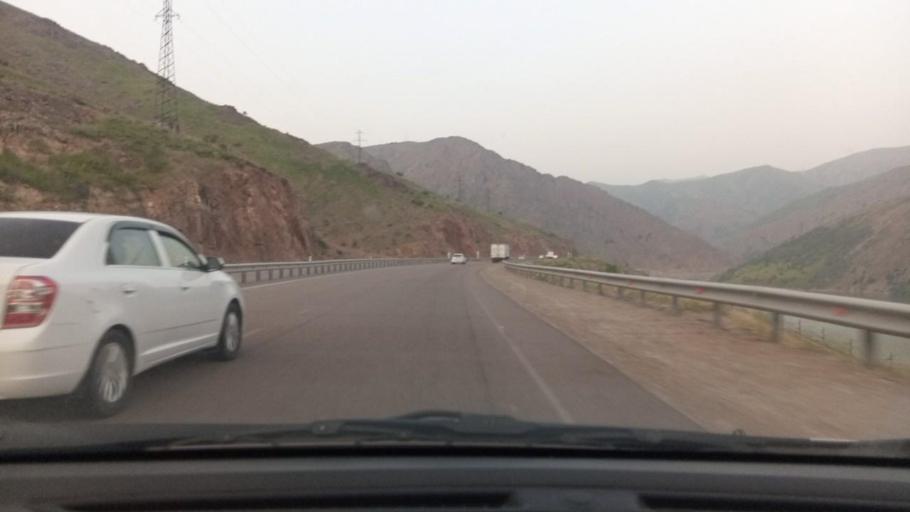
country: UZ
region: Toshkent
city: Angren
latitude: 41.0742
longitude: 70.2842
